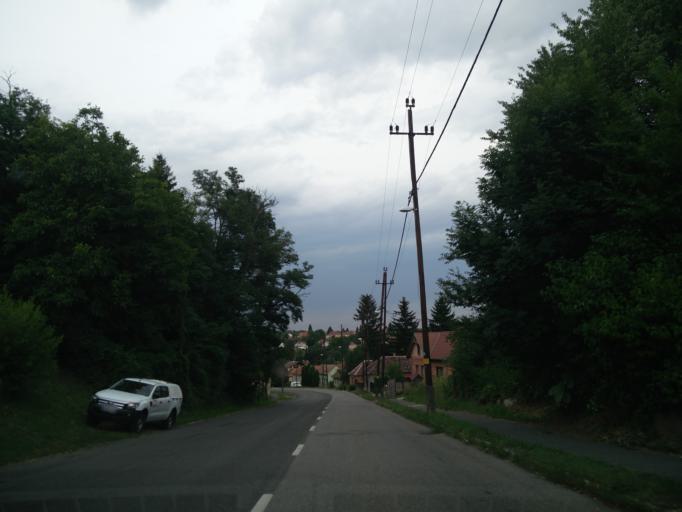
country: HU
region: Vas
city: Vasvar
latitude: 47.0449
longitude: 16.8078
